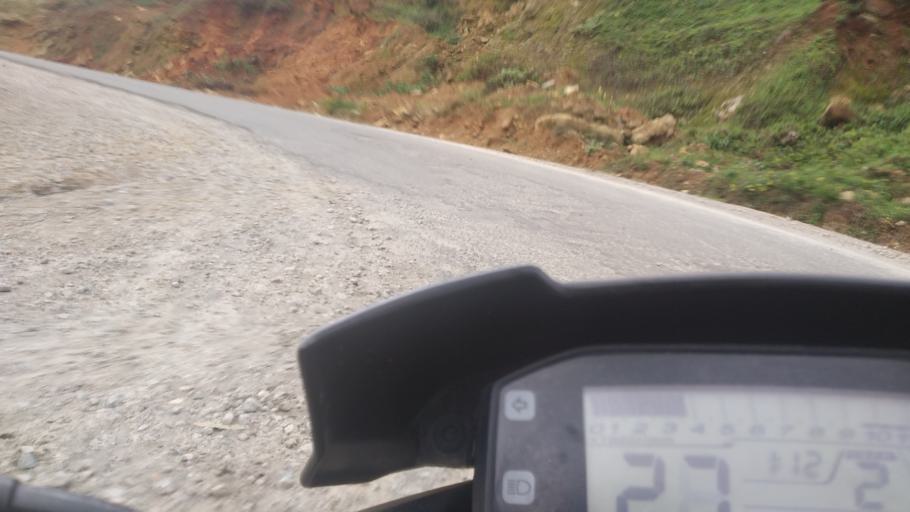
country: IN
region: Kerala
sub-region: Idukki
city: Munnar
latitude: 10.0816
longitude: 77.0753
